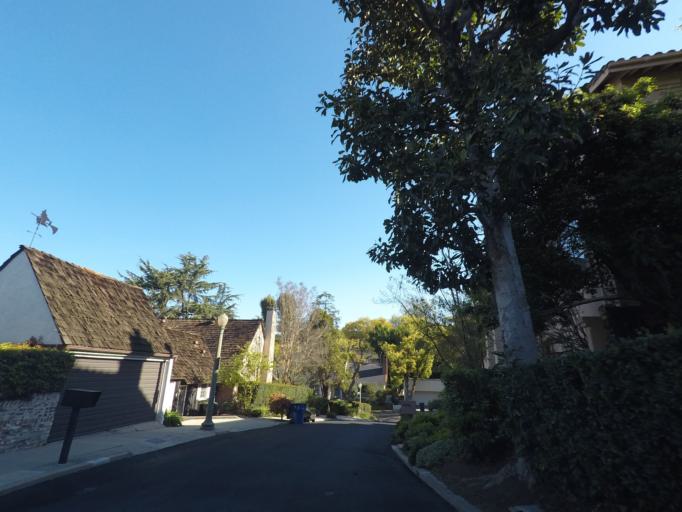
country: US
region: California
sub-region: Los Angeles County
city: Universal City
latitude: 34.1313
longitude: -118.3420
